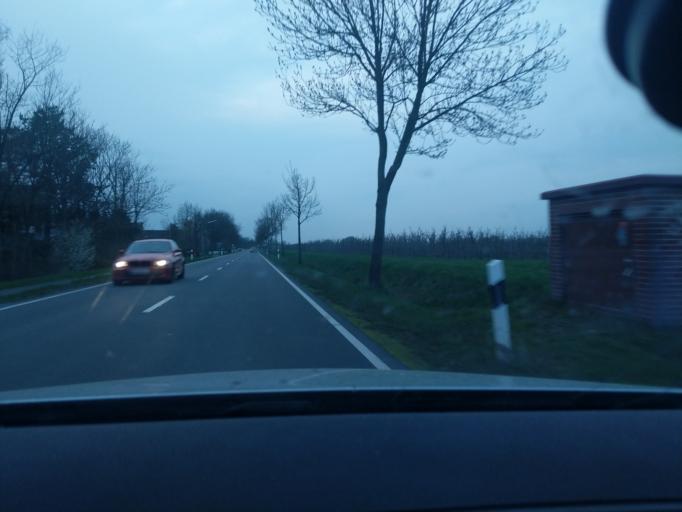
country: DE
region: Lower Saxony
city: Jork
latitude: 53.5455
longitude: 9.6748
